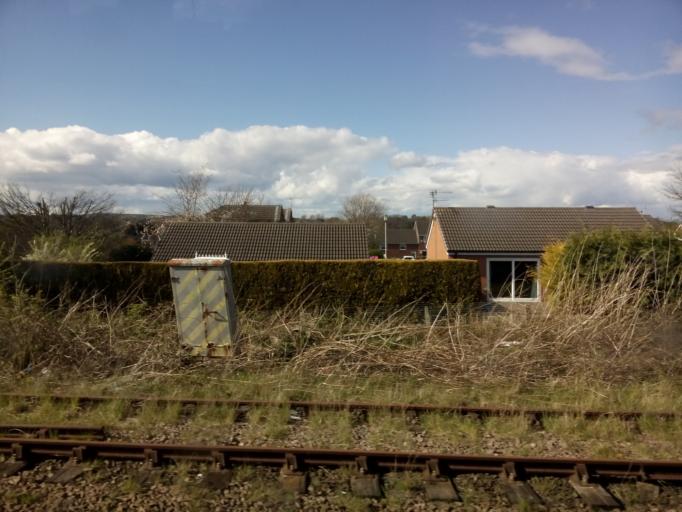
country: GB
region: England
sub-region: Northumberland
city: Morpeth
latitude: 55.1633
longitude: -1.6789
